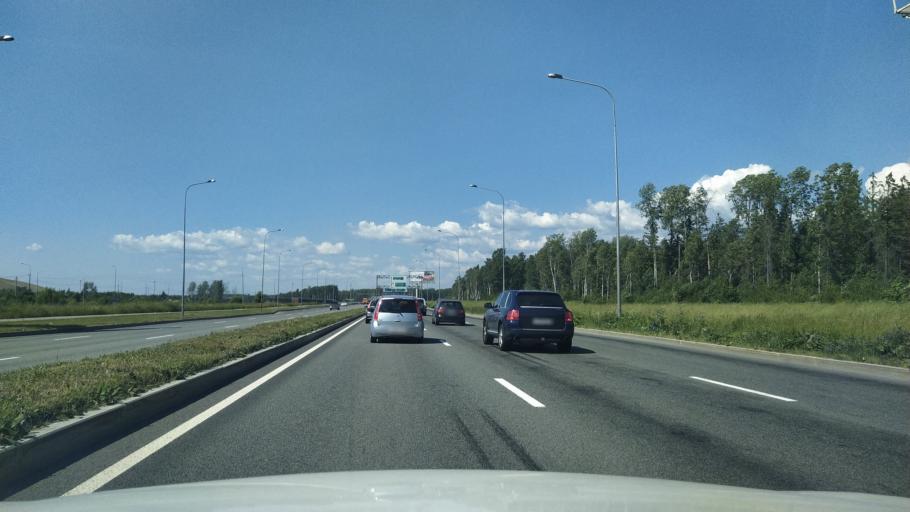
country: RU
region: St.-Petersburg
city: Levashovo
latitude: 60.0690
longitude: 30.1874
